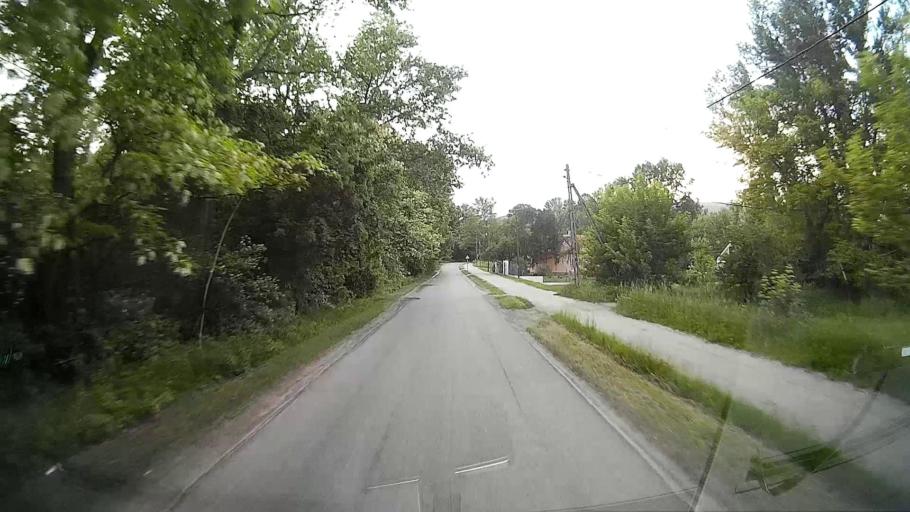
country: HU
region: Pest
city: Leanyfalu
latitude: 47.6931
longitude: 19.0952
